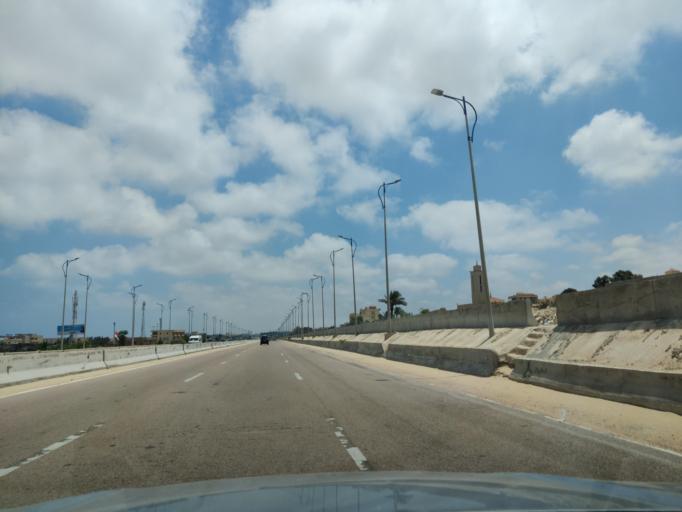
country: EG
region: Alexandria
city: Alexandria
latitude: 30.9717
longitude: 29.5647
